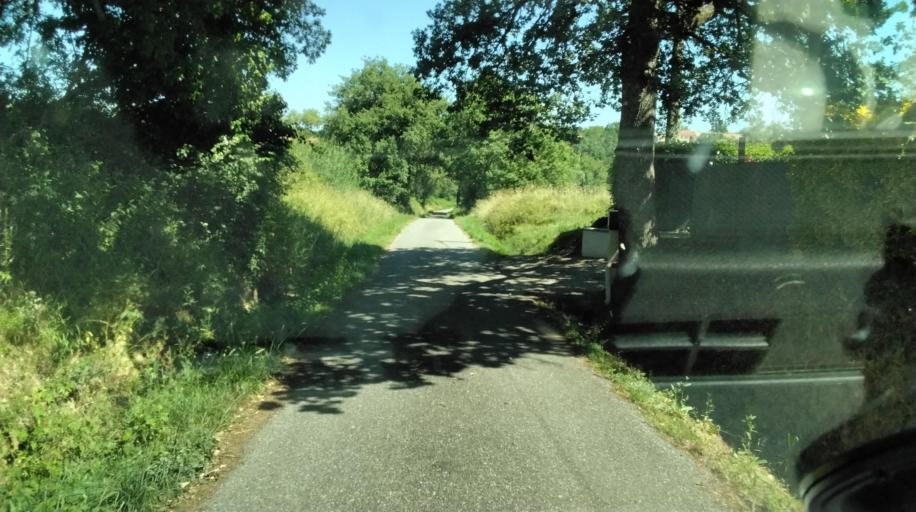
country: FR
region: Midi-Pyrenees
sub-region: Departement de la Haute-Garonne
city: Sainte-Foy-de-Peyrolieres
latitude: 43.4876
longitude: 1.1403
